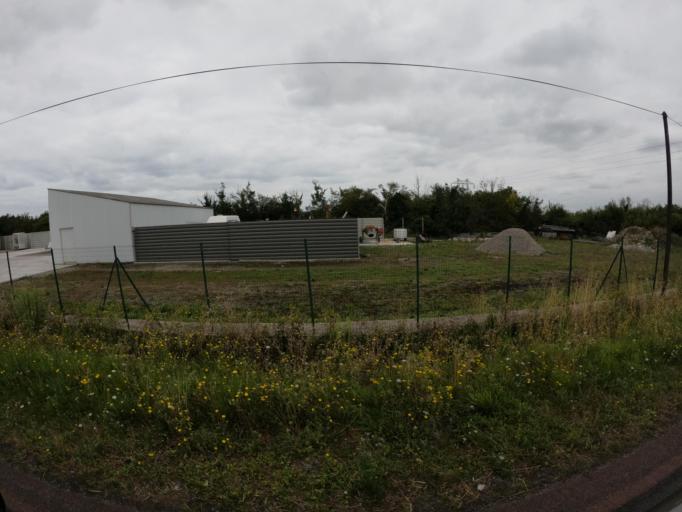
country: FR
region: Pays de la Loire
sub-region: Departement de la Vendee
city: Saint-Michel-le-Cloucq
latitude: 46.4346
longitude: -0.7373
